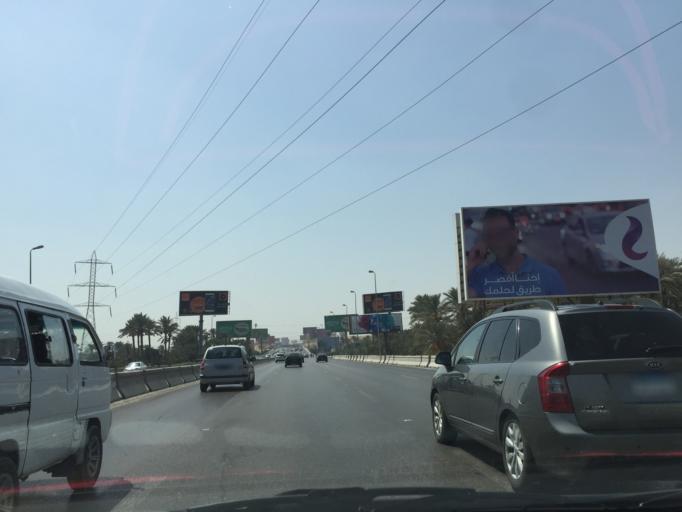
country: EG
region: Al Jizah
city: Awsim
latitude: 30.0603
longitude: 31.0855
